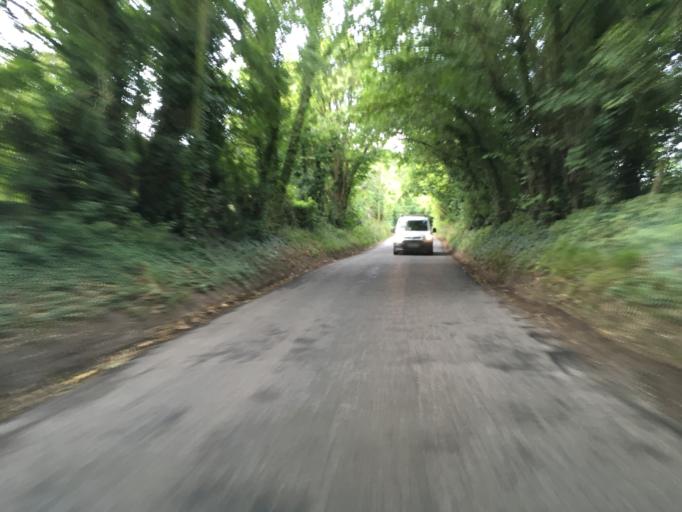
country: GB
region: England
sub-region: Hampshire
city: Colden Common
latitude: 50.9938
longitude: -1.2725
